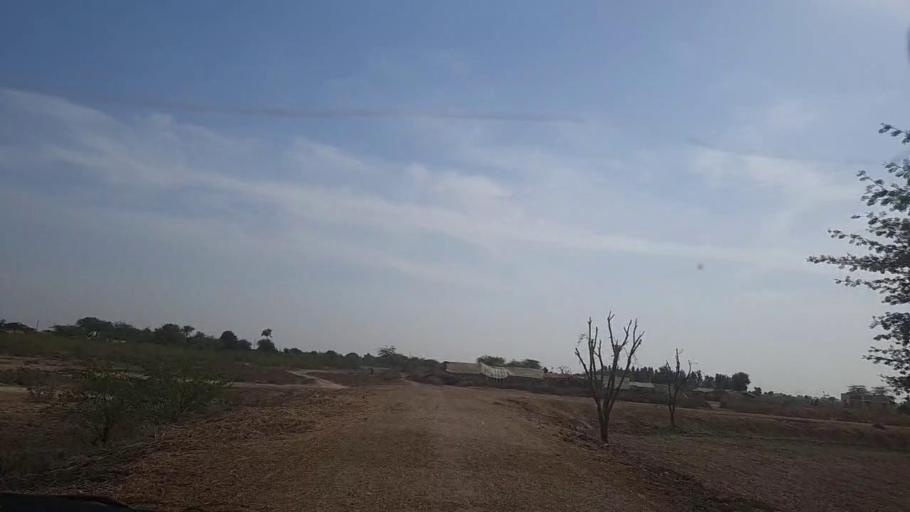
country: PK
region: Sindh
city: Pithoro
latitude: 25.5465
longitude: 69.3558
